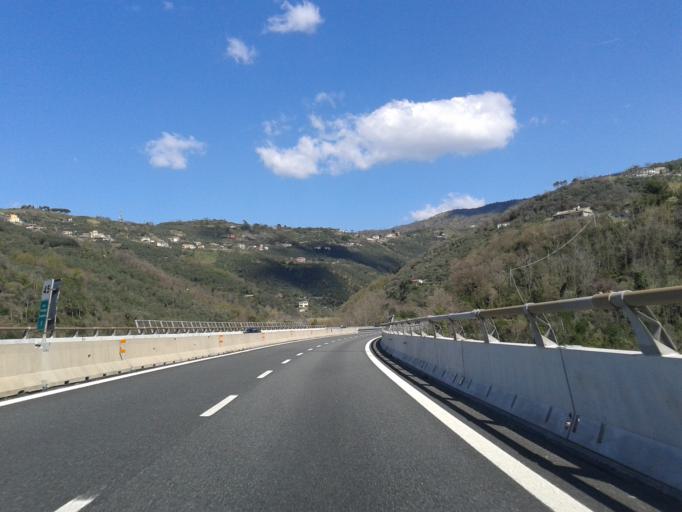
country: IT
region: Liguria
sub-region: Provincia di Genova
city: Sestri Levante
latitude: 44.2956
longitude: 9.3839
